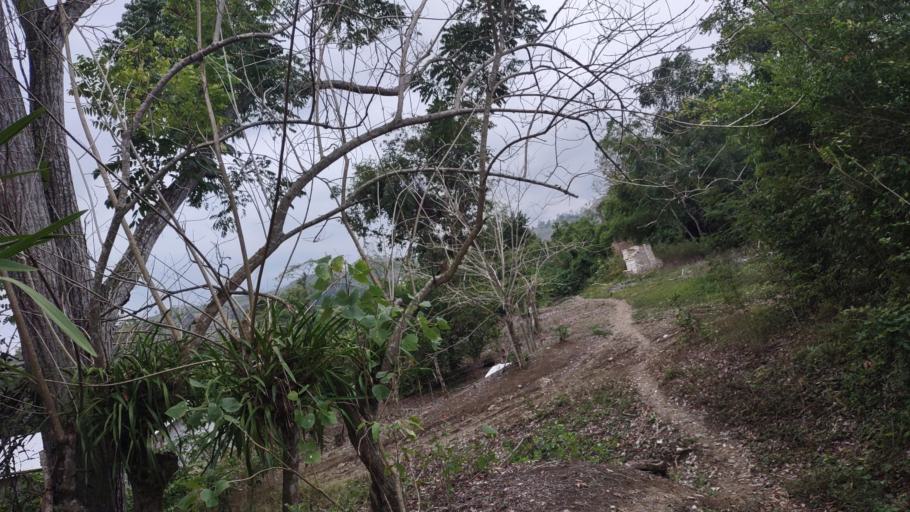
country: MX
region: Veracruz
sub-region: Coatzintla
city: Manuel Maria Contreras
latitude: 20.4108
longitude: -97.4552
